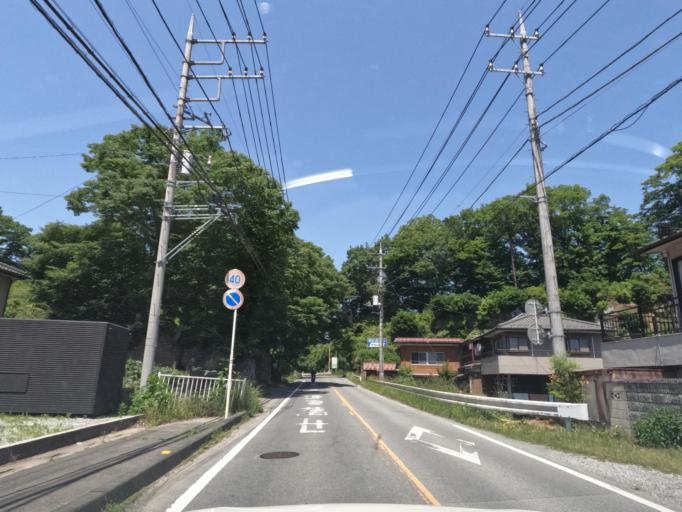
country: JP
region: Saitama
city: Chichibu
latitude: 36.0215
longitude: 139.1066
